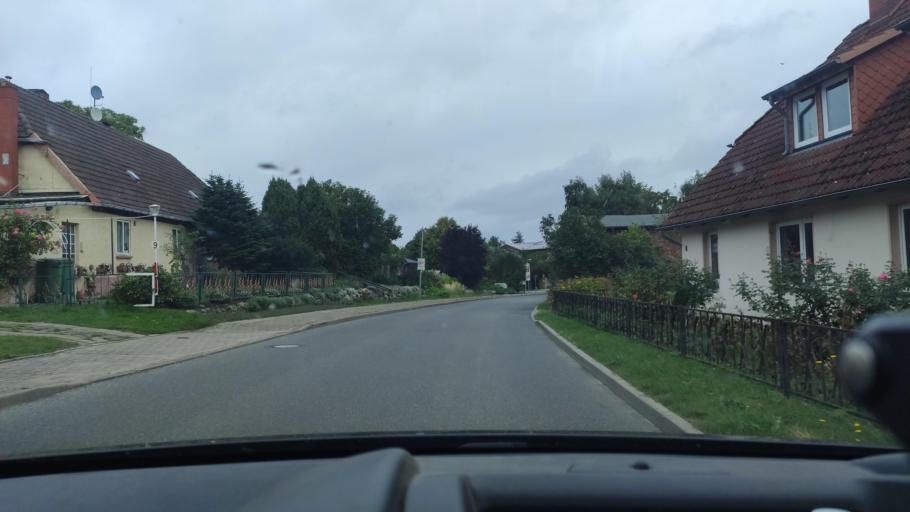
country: DE
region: Mecklenburg-Vorpommern
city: Guestrow
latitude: 53.8450
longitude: 12.0934
